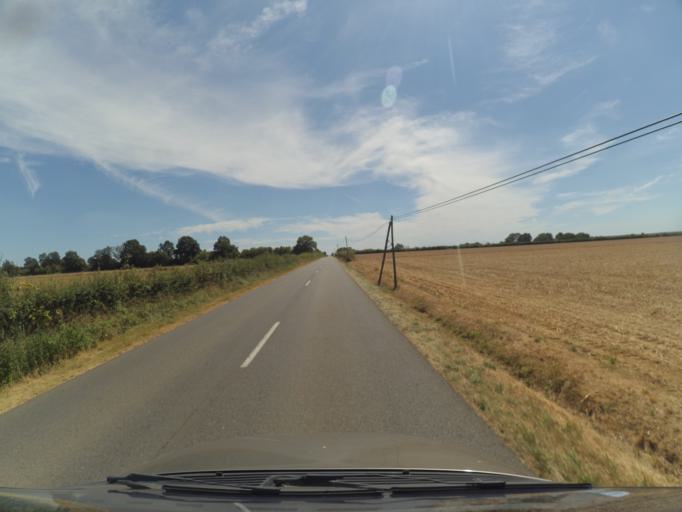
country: FR
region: Poitou-Charentes
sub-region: Departement de la Vienne
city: Usson-du-Poitou
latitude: 46.1770
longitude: 0.5440
